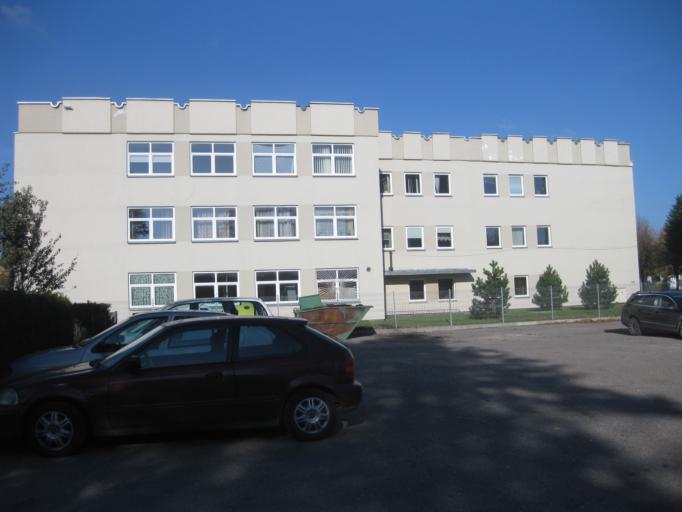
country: LT
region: Kauno apskritis
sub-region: Kauno rajonas
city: Garliava
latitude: 54.8353
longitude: 23.8671
